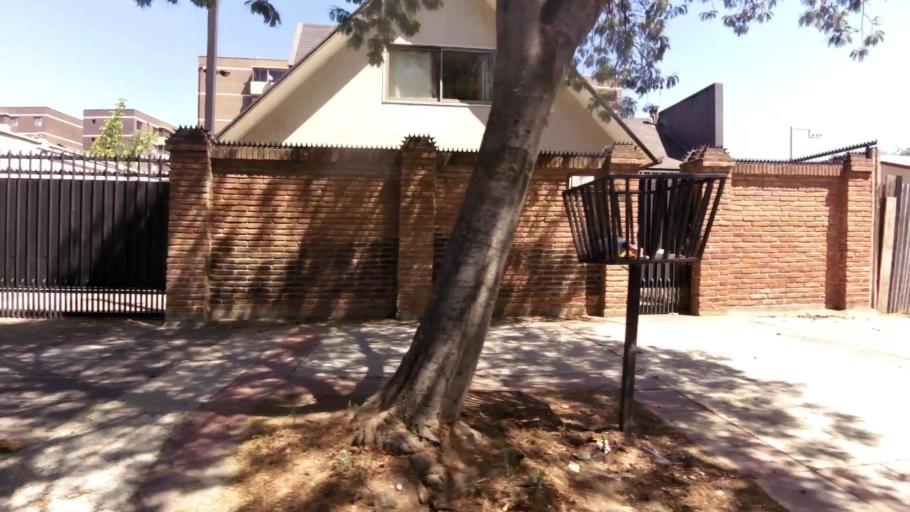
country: CL
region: Maule
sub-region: Provincia de Talca
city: Talca
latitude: -35.4170
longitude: -71.6600
